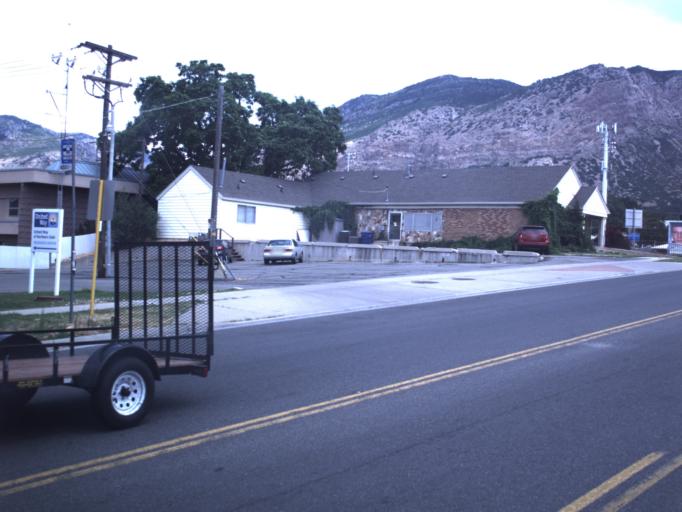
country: US
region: Utah
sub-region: Weber County
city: Ogden
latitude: 41.2099
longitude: -111.9495
